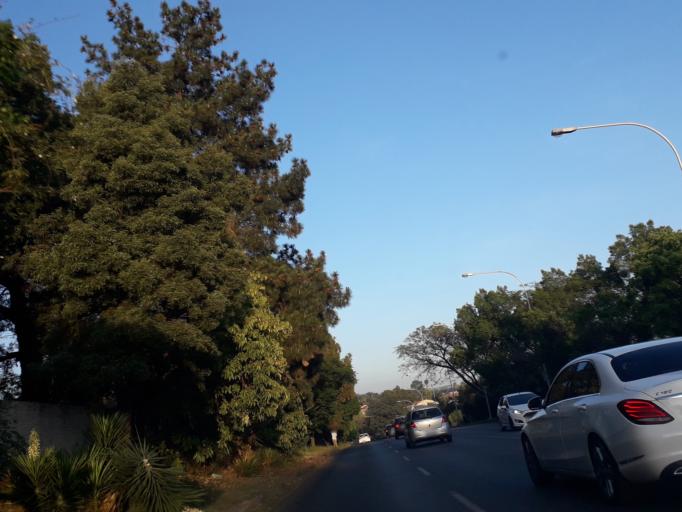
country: ZA
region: Gauteng
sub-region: City of Johannesburg Metropolitan Municipality
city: Modderfontein
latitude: -26.1267
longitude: 28.1144
